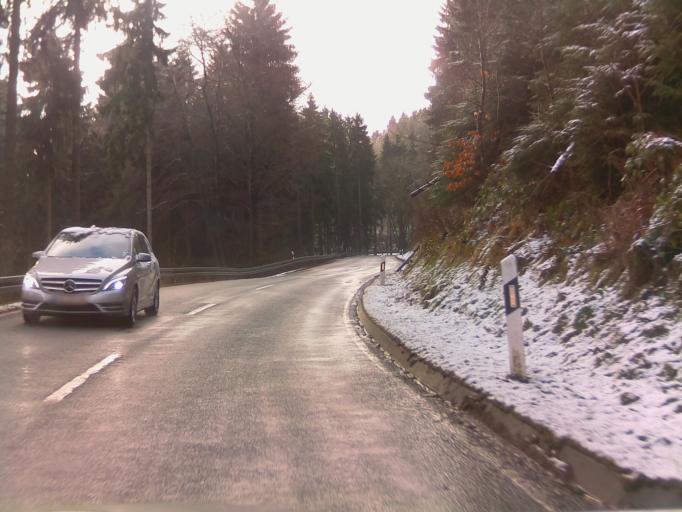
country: DE
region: Thuringia
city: Frankenhain
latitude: 50.7654
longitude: 10.7700
